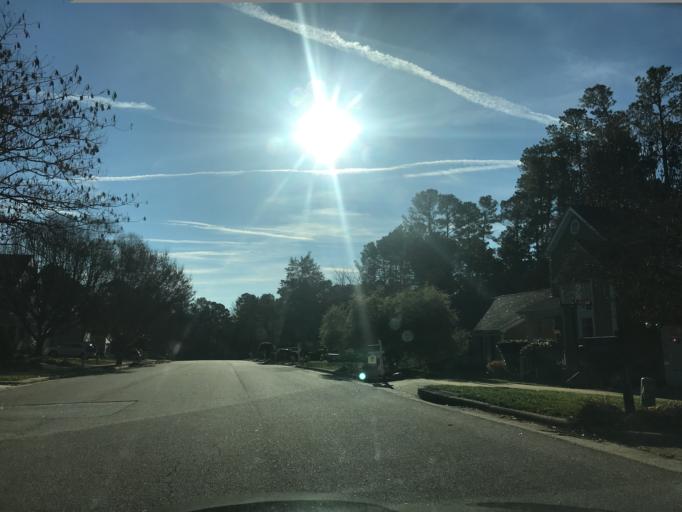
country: US
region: North Carolina
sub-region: Wake County
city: West Raleigh
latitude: 35.8894
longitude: -78.5975
